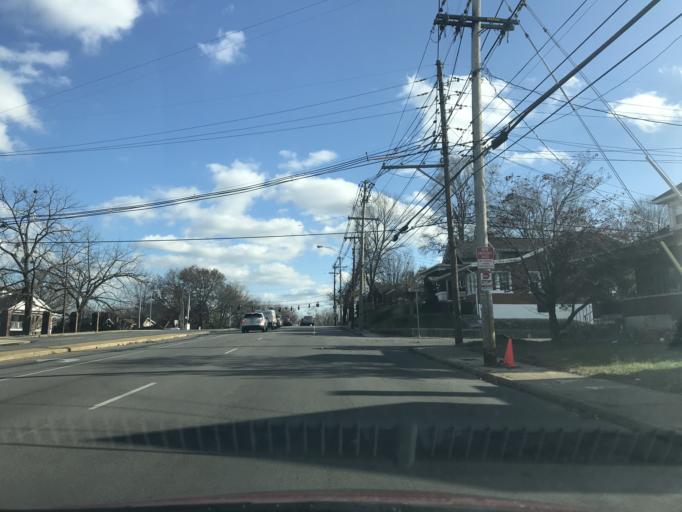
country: US
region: Kentucky
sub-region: Jefferson County
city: Audubon Park
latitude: 38.2248
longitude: -85.7314
